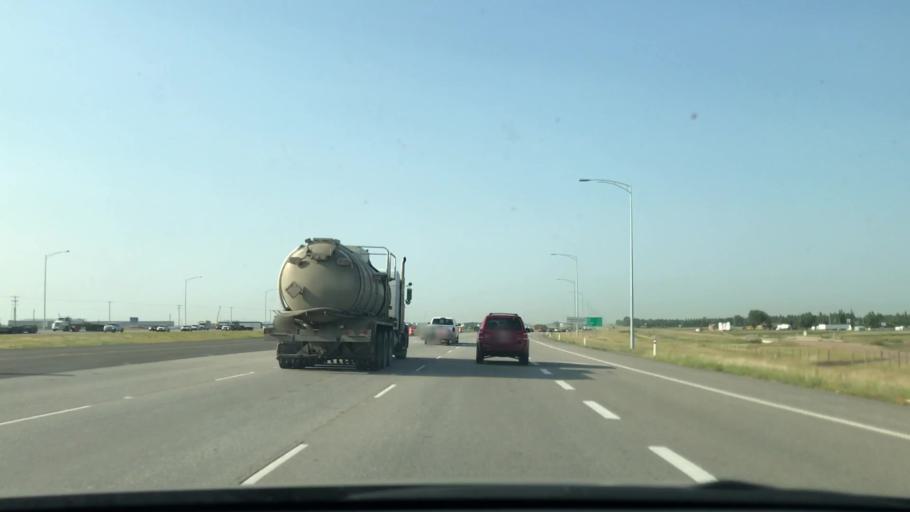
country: CA
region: Alberta
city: Beaumont
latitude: 53.3893
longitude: -113.5161
